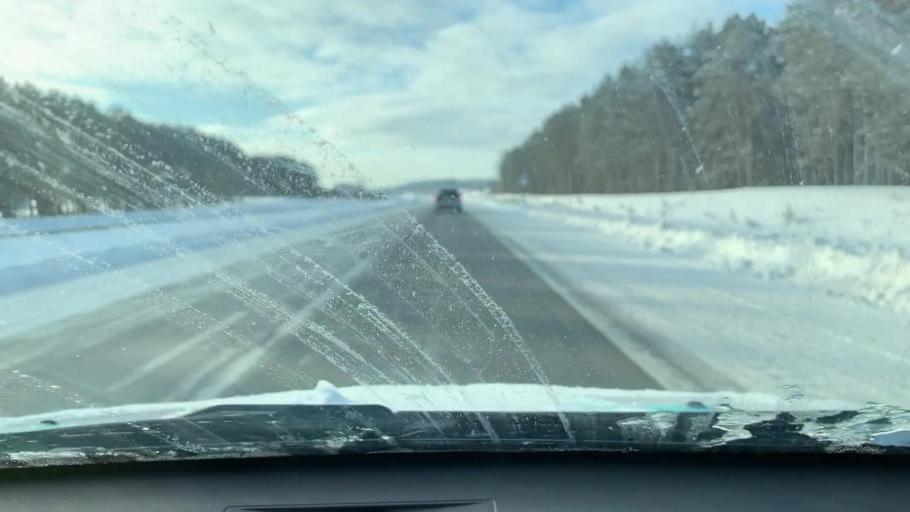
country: US
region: Michigan
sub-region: Wexford County
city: Cadillac
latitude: 44.2771
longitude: -85.3886
